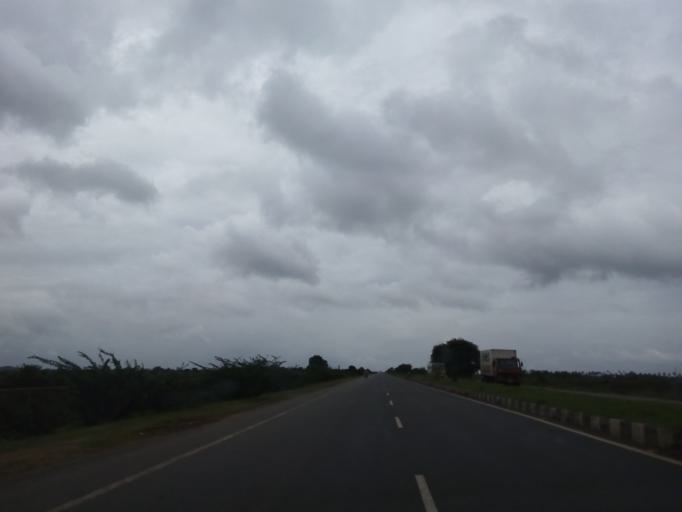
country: IN
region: Karnataka
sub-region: Haveri
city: Haveri
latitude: 14.7505
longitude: 75.4498
